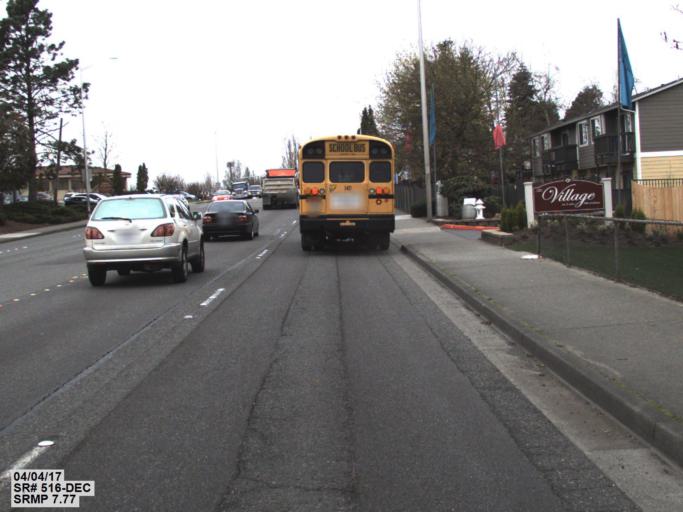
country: US
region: Washington
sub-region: King County
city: Kent
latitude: 47.3697
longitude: -122.1945
